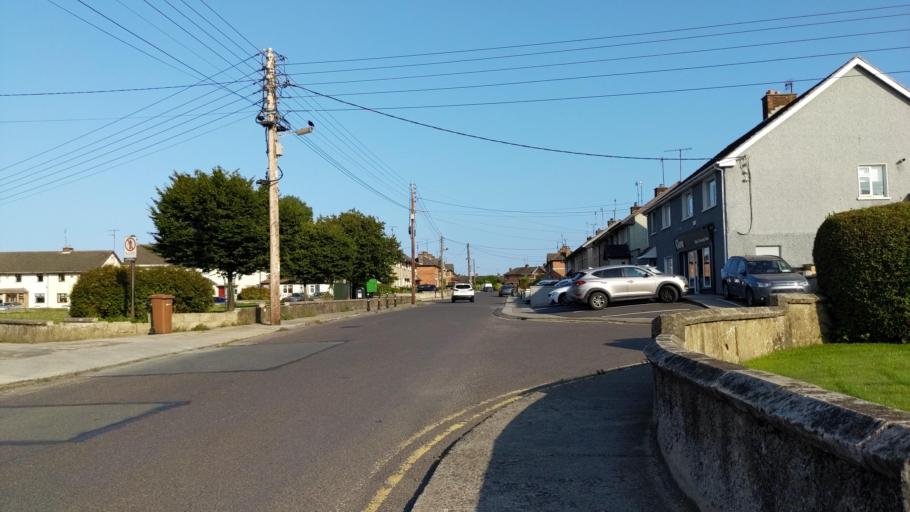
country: IE
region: Leinster
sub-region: Lu
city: Drogheda
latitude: 53.7085
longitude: -6.3568
